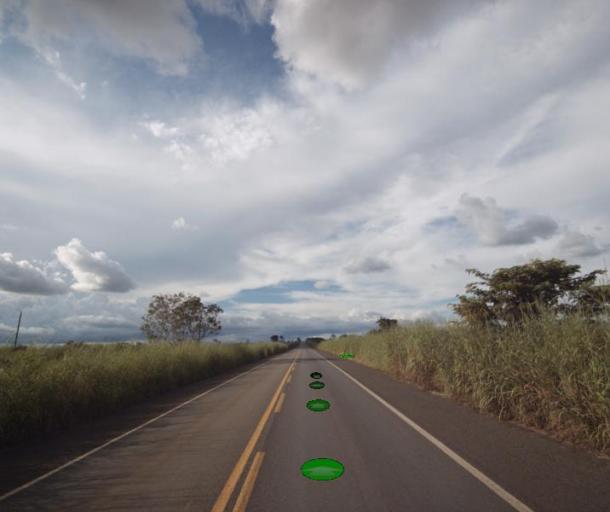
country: BR
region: Goias
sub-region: Niquelandia
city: Niquelandia
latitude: -14.7614
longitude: -48.6226
